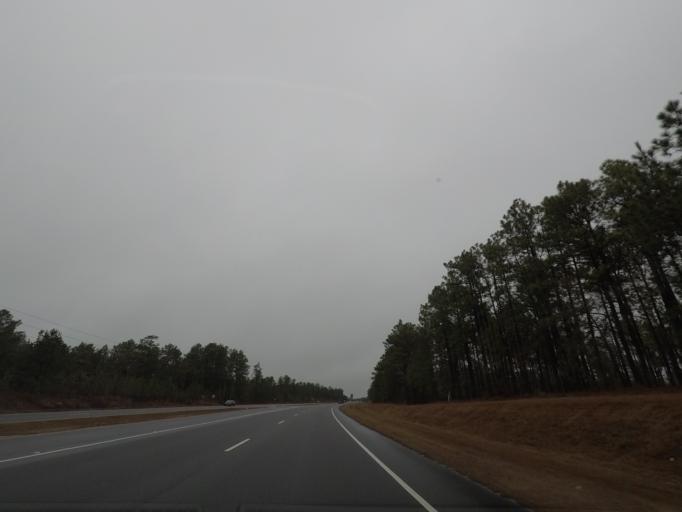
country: US
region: North Carolina
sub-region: Cumberland County
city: Spring Lake
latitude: 35.2351
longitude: -79.0196
